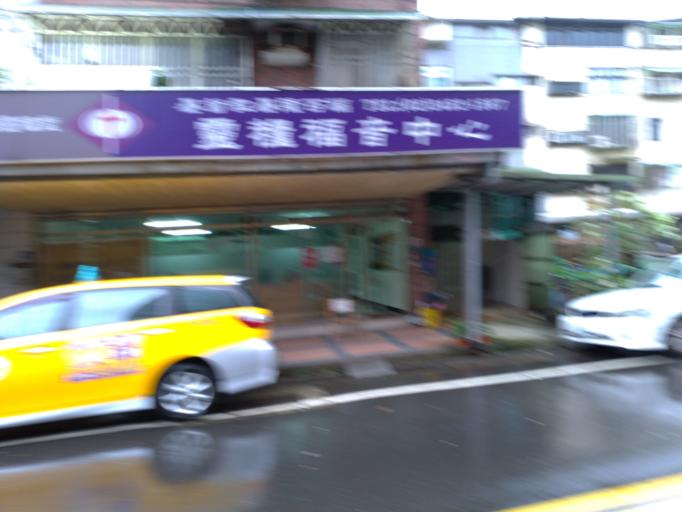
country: TW
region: Taiwan
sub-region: Keelung
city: Keelung
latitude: 25.0855
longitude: 121.6959
